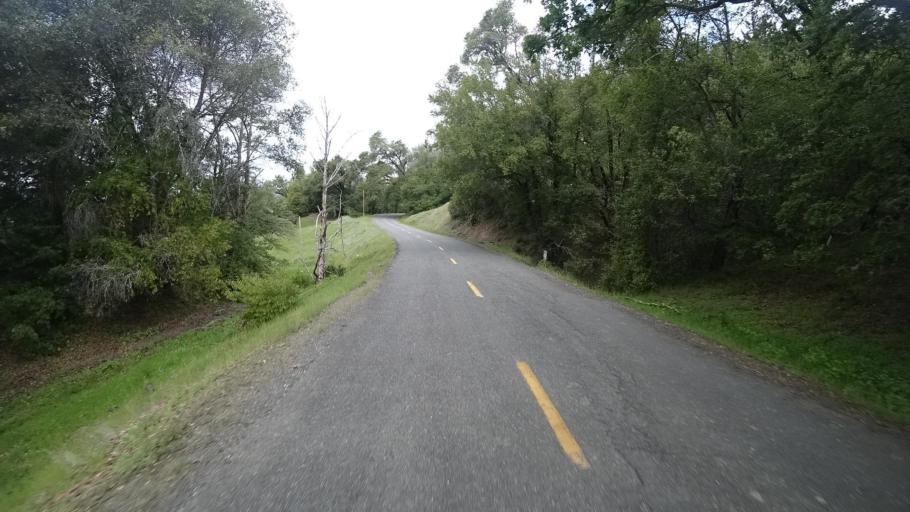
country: US
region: California
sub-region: Humboldt County
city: Redway
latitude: 40.2318
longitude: -123.6166
